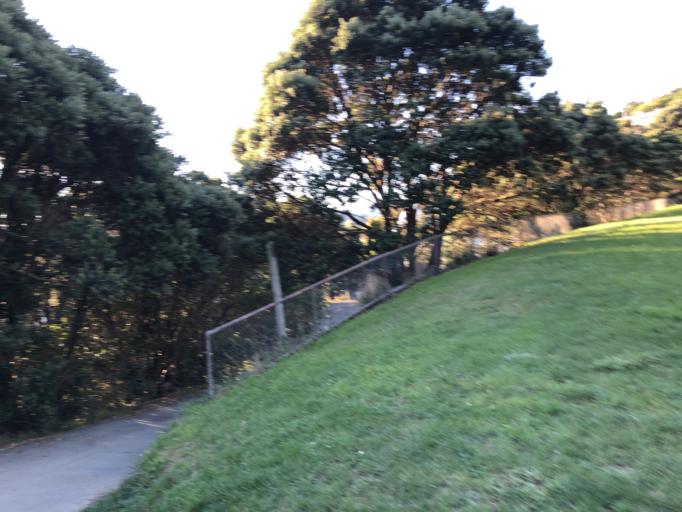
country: NZ
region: Wellington
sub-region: Wellington City
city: Wellington
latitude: -41.2968
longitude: 174.7900
